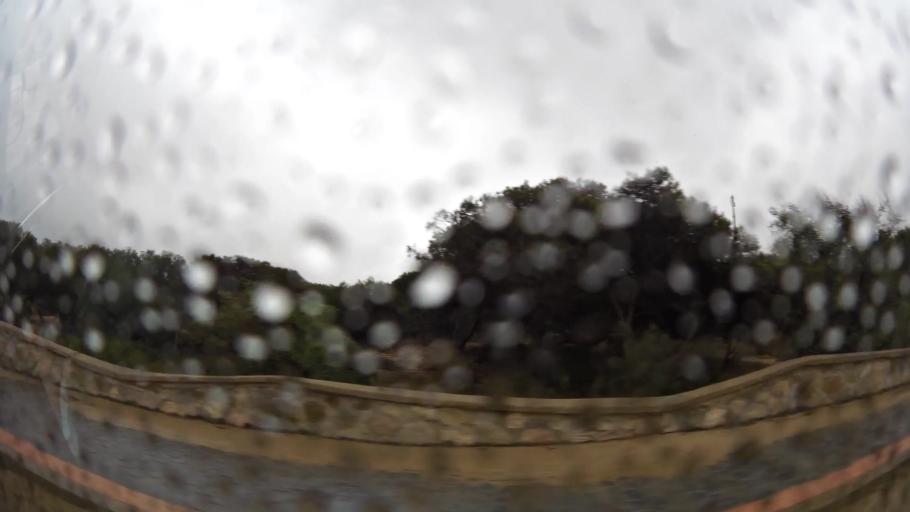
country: MA
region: Taza-Al Hoceima-Taounate
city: Al Hoceima
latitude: 35.2512
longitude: -3.9451
